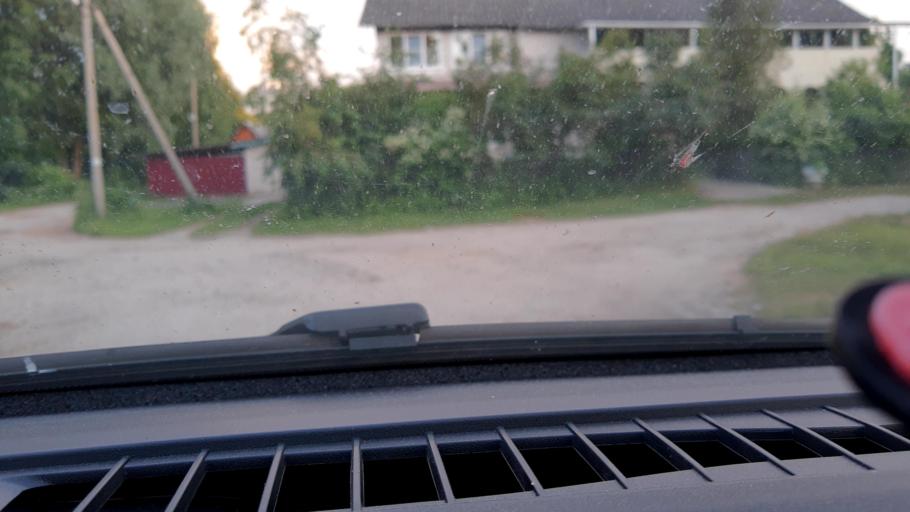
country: RU
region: Nizjnij Novgorod
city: Afonino
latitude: 56.3173
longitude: 44.2024
